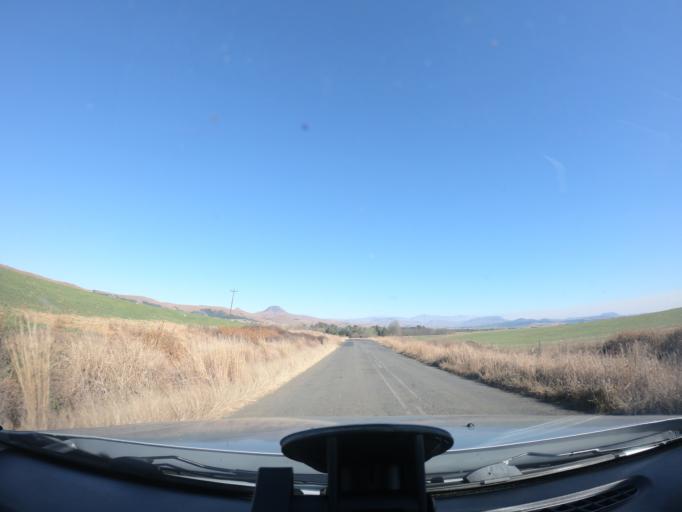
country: ZA
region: KwaZulu-Natal
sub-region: uMgungundlovu District Municipality
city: Mooirivier
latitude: -29.3267
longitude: 29.8525
